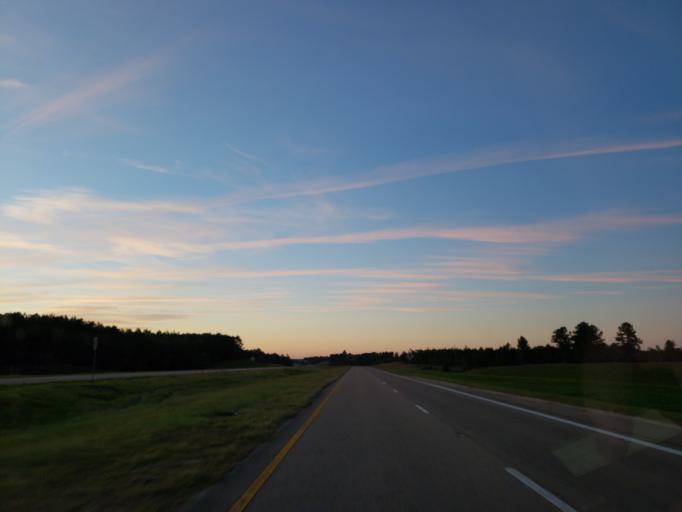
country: US
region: Mississippi
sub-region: Wayne County
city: Waynesboro
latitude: 31.7090
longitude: -88.6272
